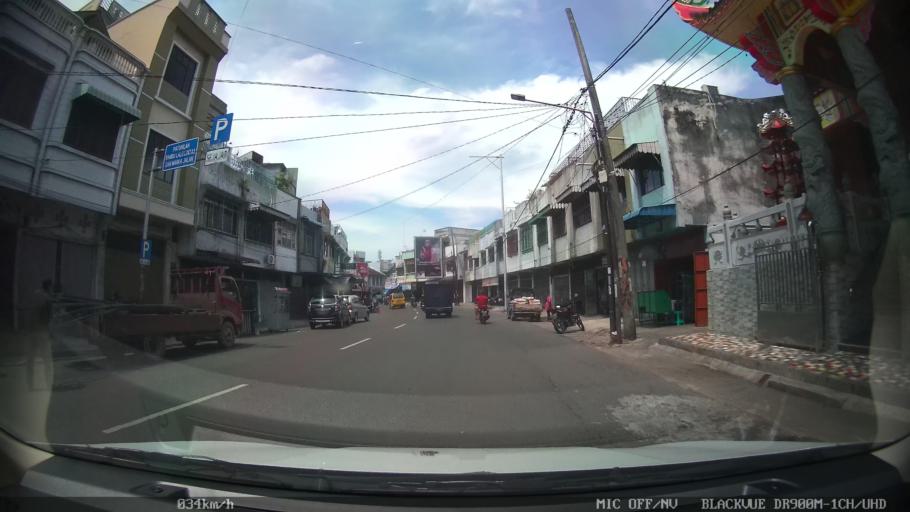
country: ID
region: North Sumatra
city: Binjai
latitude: 3.6080
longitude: 98.4913
